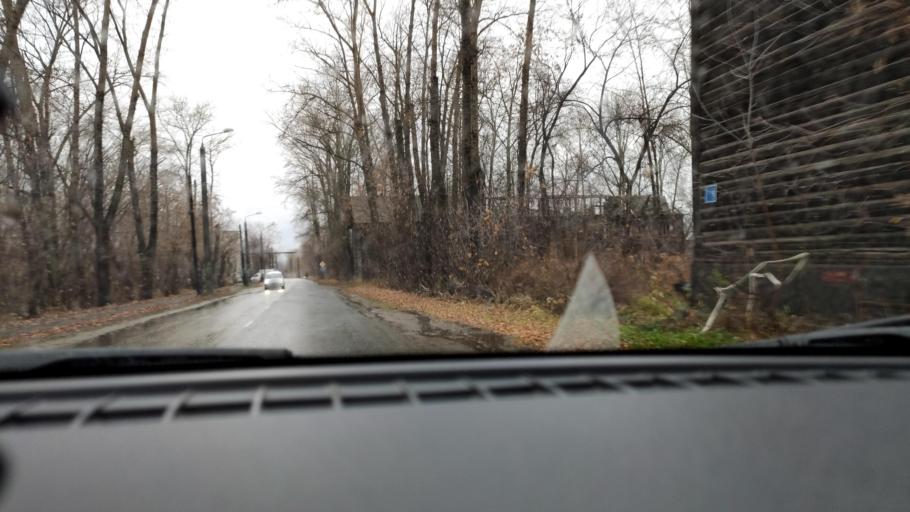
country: RU
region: Perm
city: Perm
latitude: 58.0941
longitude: 56.3766
